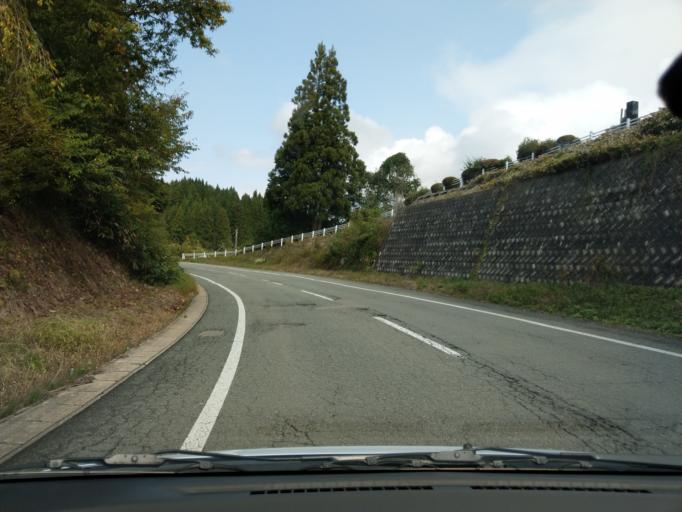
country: JP
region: Akita
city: Omagari
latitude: 39.5069
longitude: 140.3127
